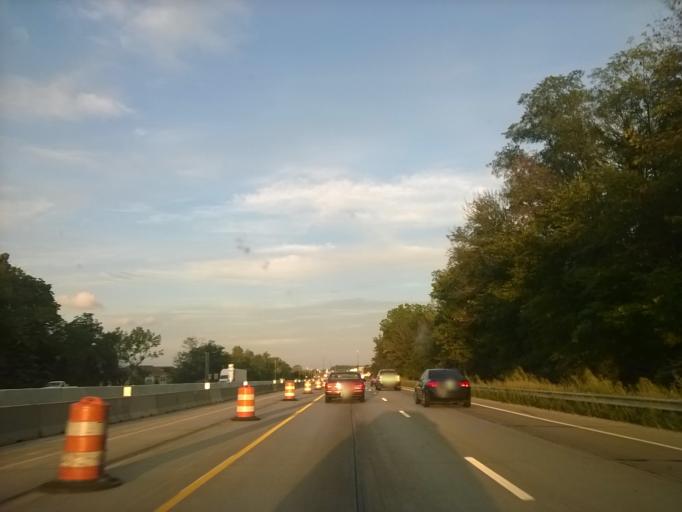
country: US
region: Indiana
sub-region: Marion County
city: Beech Grove
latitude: 39.7039
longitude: -86.0958
